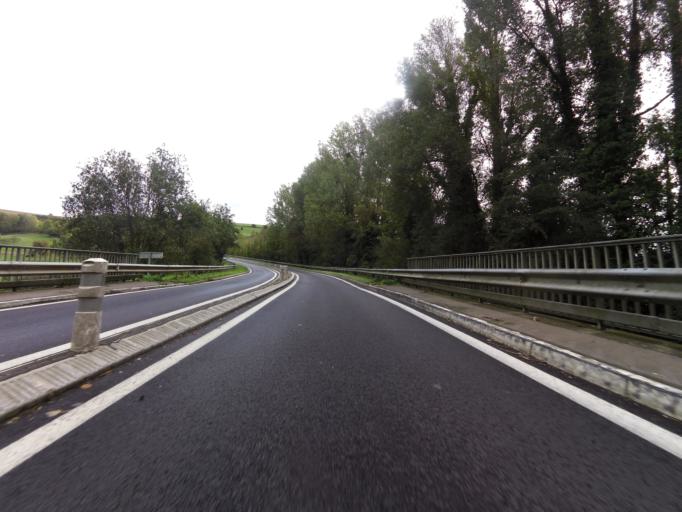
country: FR
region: Haute-Normandie
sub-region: Departement de la Seine-Maritime
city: Criel-sur-Mer
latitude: 50.0100
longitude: 1.3187
